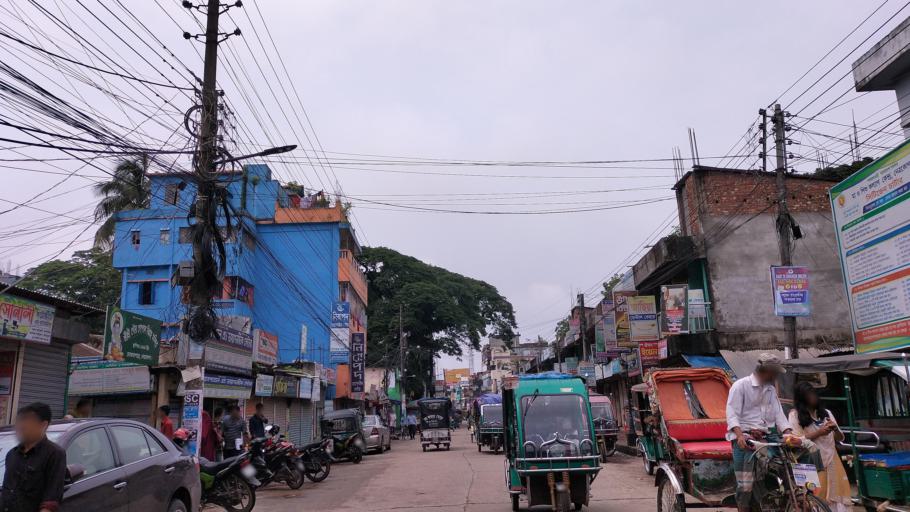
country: BD
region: Dhaka
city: Netrakona
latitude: 24.8797
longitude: 90.7314
